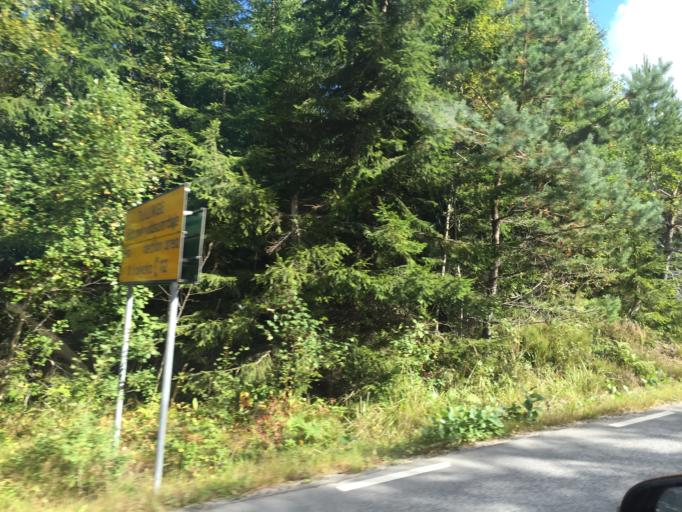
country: SE
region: Stockholm
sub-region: Botkyrka Kommun
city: Tullinge
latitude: 59.1685
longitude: 17.9075
